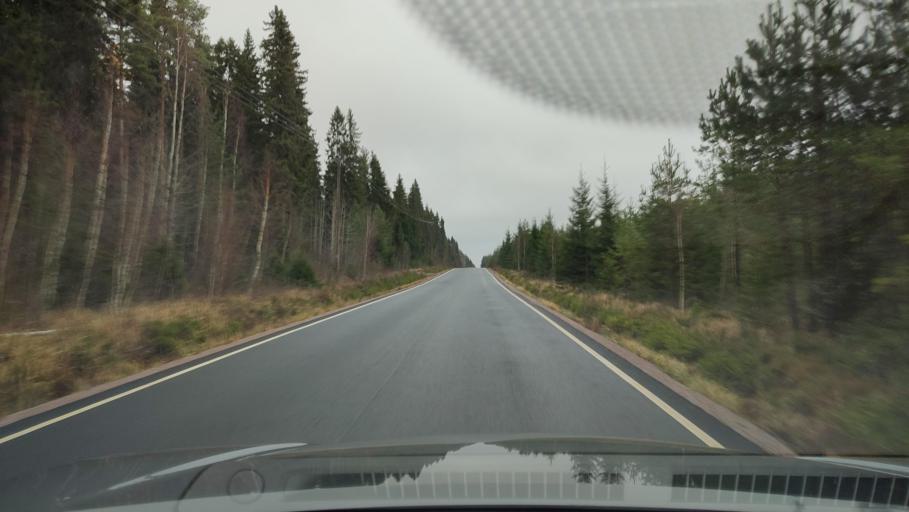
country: FI
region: Southern Ostrobothnia
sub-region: Suupohja
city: Karijoki
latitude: 62.1504
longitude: 21.7037
